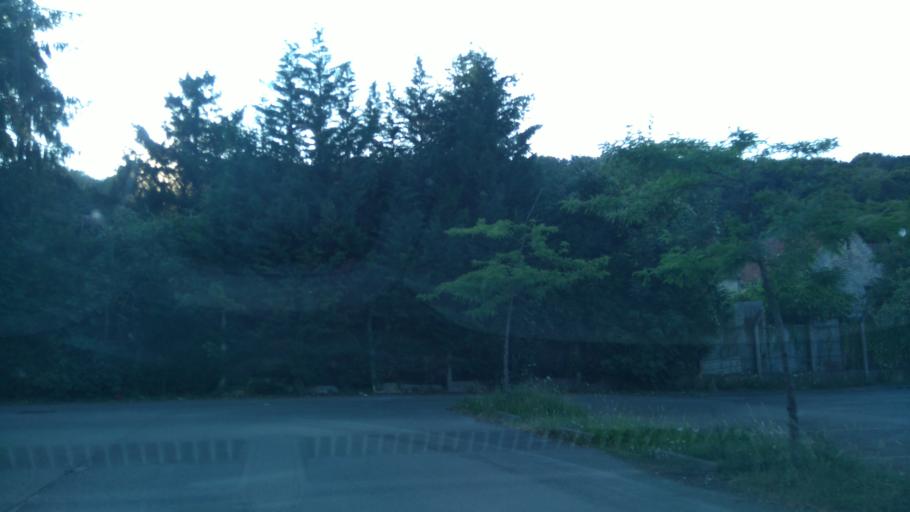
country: FR
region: Picardie
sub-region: Departement de l'Oise
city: Montataire
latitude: 49.2610
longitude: 2.4512
